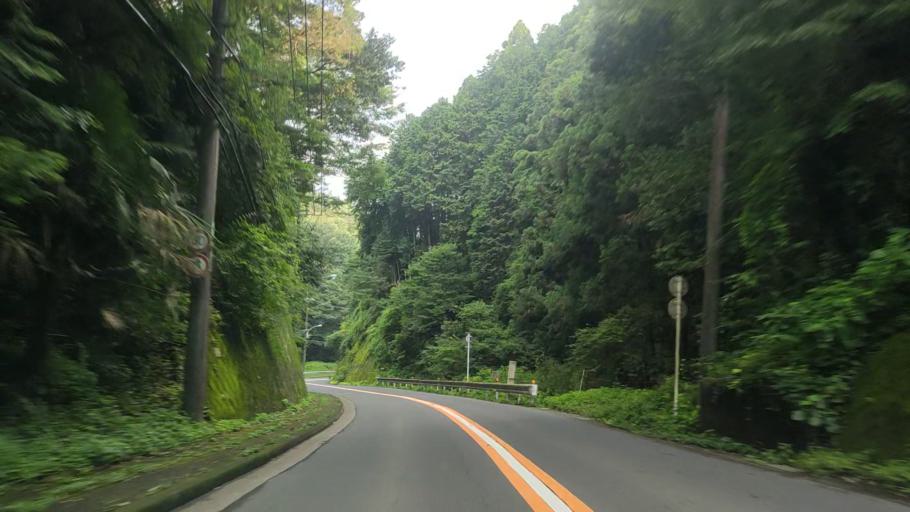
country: JP
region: Saitama
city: Hanno
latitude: 35.8257
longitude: 139.2740
